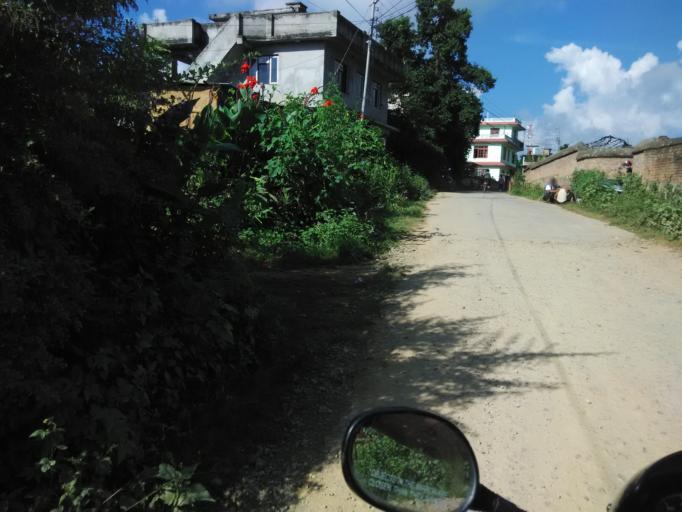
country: NP
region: Central Region
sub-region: Bagmati Zone
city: Patan
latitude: 27.6073
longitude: 85.3403
